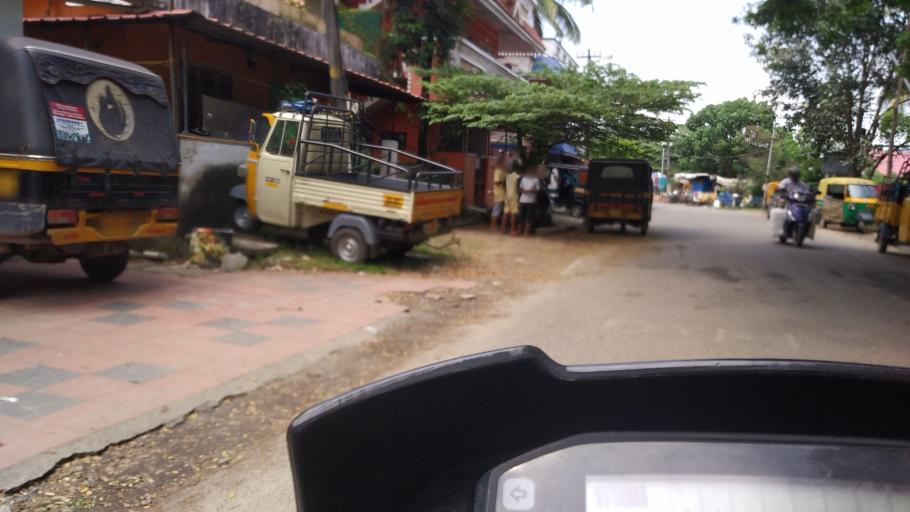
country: IN
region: Kerala
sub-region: Ernakulam
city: Cochin
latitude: 9.9739
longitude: 76.2931
